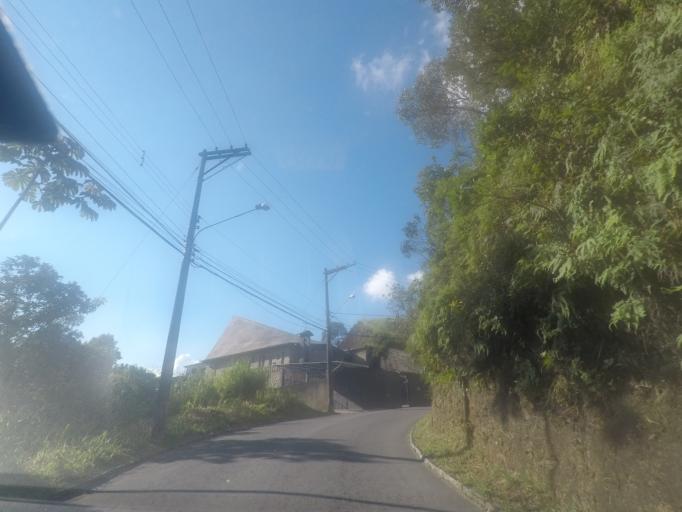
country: BR
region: Rio de Janeiro
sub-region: Petropolis
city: Petropolis
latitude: -22.5053
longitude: -43.1555
